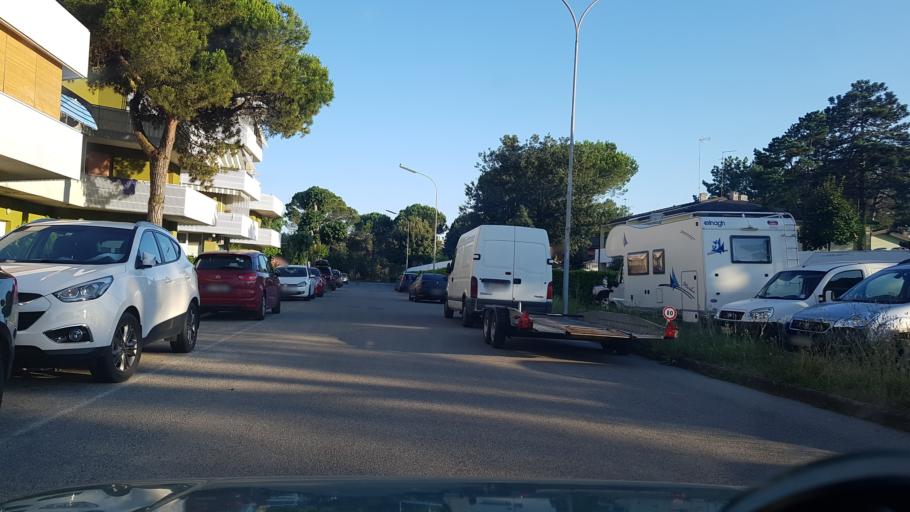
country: IT
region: Veneto
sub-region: Provincia di Venezia
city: Bibione
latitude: 45.6391
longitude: 13.0426
